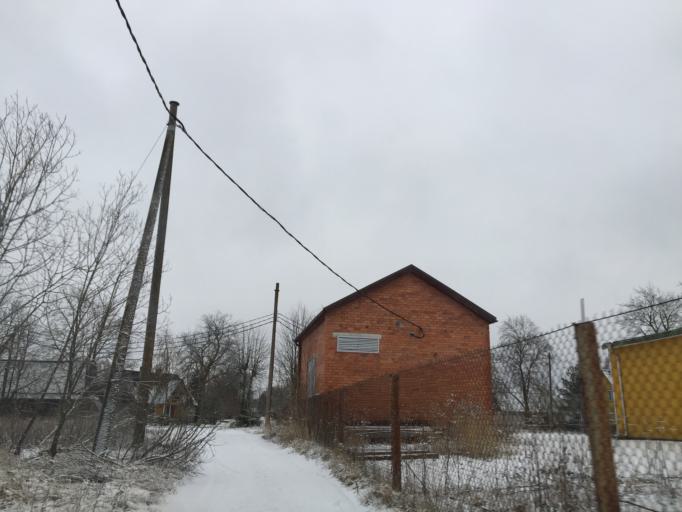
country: EE
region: Laeaene
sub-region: Lihula vald
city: Lihula
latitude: 58.6855
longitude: 23.8341
